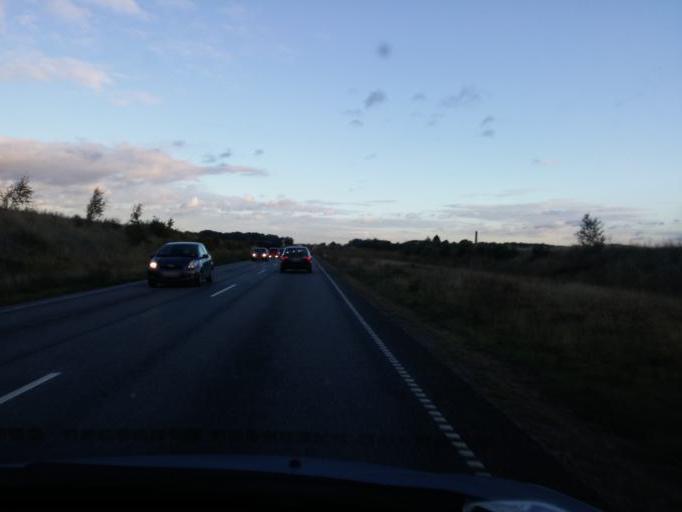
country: DK
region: South Denmark
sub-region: Odense Kommune
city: Bullerup
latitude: 55.4004
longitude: 10.4748
